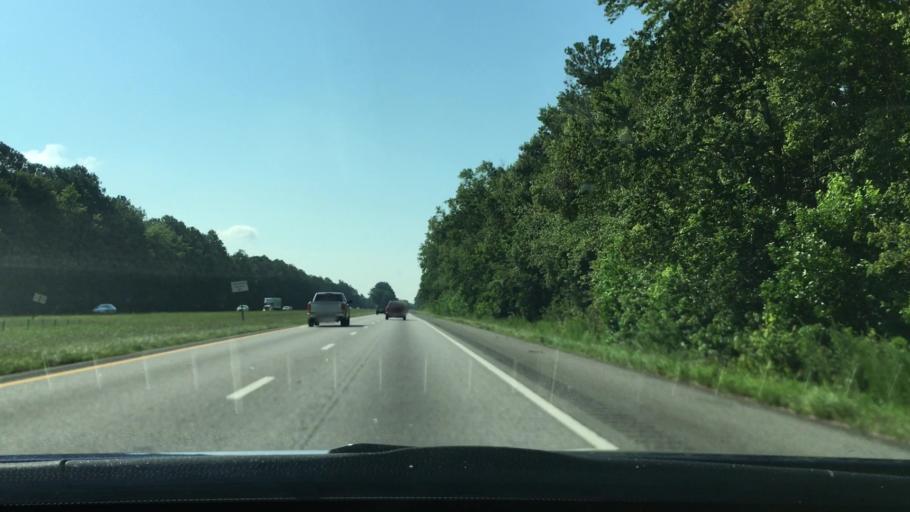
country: US
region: South Carolina
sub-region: Dorchester County
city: Ridgeville
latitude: 33.1798
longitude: -80.3769
